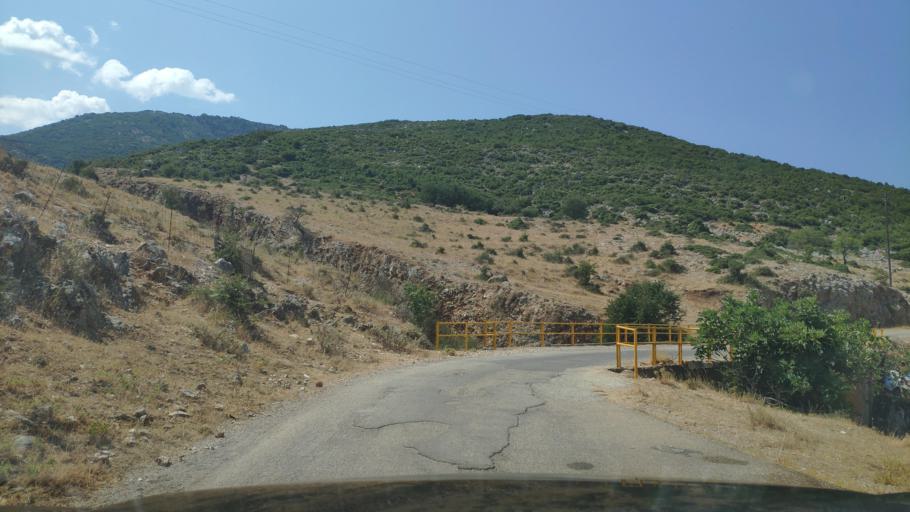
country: GR
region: West Greece
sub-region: Nomos Aitolias kai Akarnanias
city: Monastirakion
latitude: 38.8442
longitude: 20.9429
